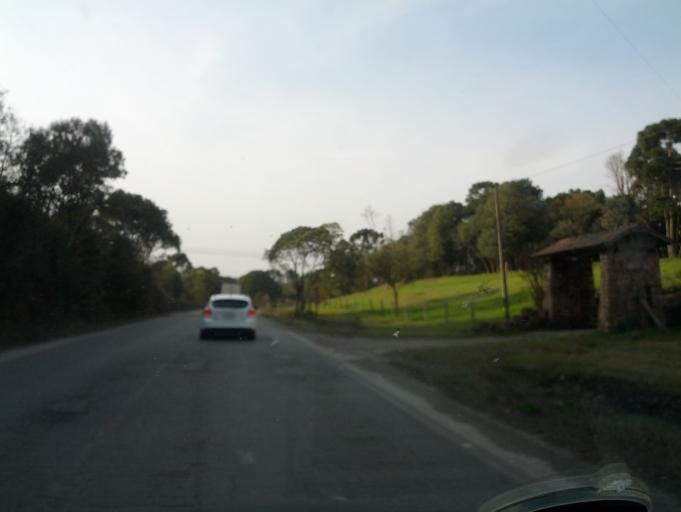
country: BR
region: Santa Catarina
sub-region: Otacilio Costa
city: Otacilio Costa
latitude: -27.5595
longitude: -50.1497
